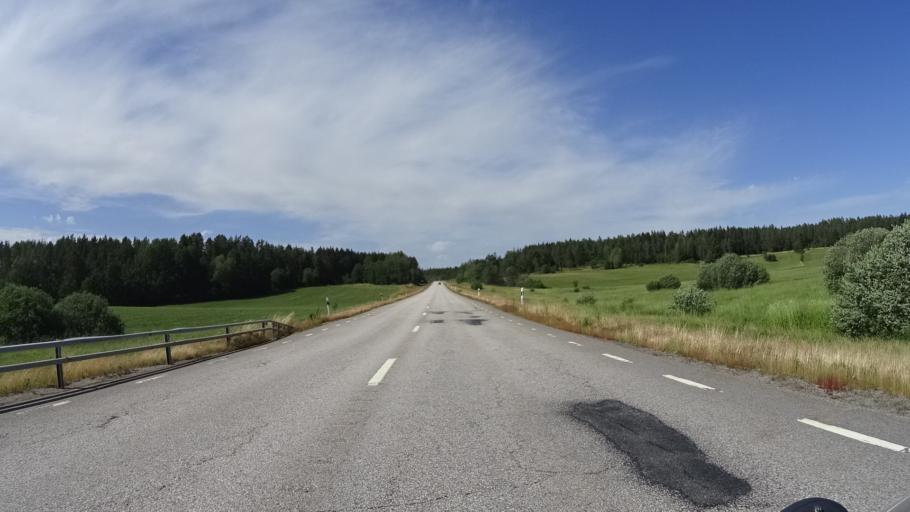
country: SE
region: Kalmar
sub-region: Vasterviks Kommun
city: Gamleby
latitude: 57.9471
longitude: 16.3816
